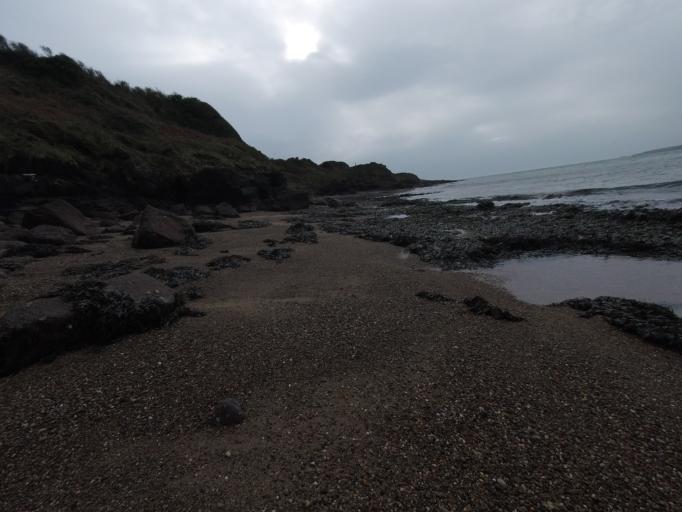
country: IE
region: Munster
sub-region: Waterford
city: Tra Mhor
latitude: 52.1389
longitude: -7.0988
